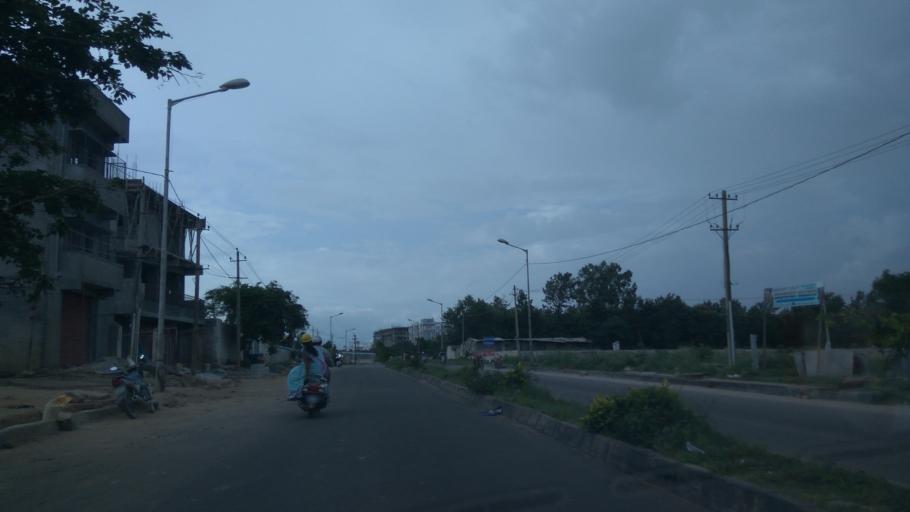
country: IN
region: Karnataka
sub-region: Bangalore Urban
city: Yelahanka
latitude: 13.1093
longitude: 77.6335
